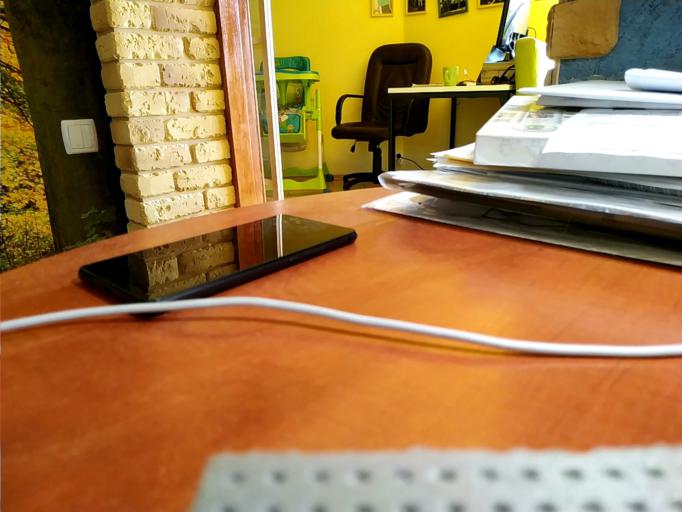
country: RU
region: Tverskaya
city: Kalashnikovo
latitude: 57.3839
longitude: 35.3323
